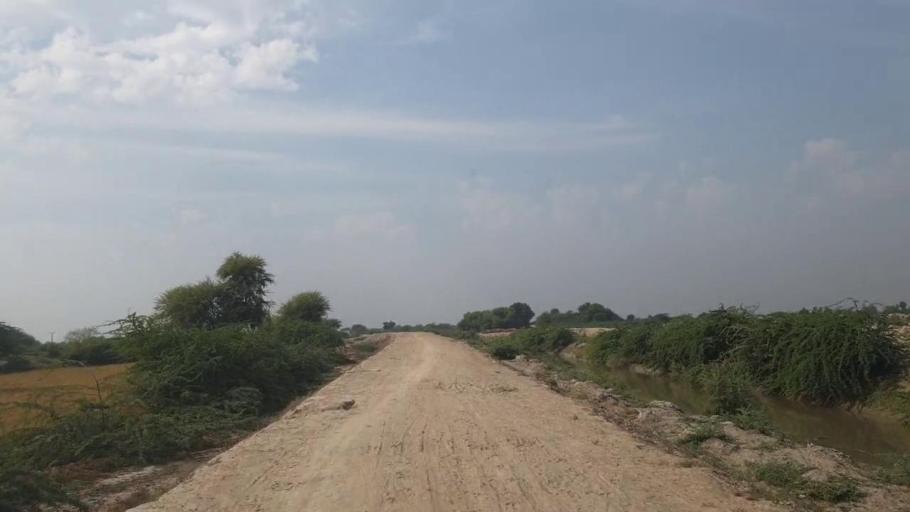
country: PK
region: Sindh
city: Rajo Khanani
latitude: 24.9680
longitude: 69.0071
